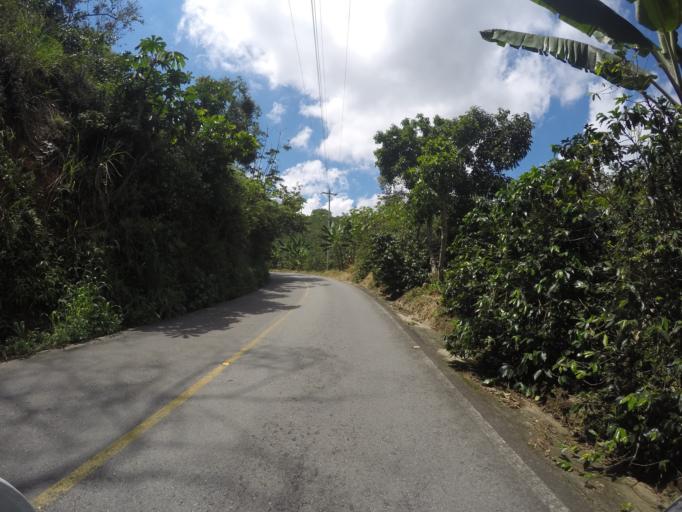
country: CO
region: Quindio
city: Quimbaya
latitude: 4.6265
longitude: -75.7402
